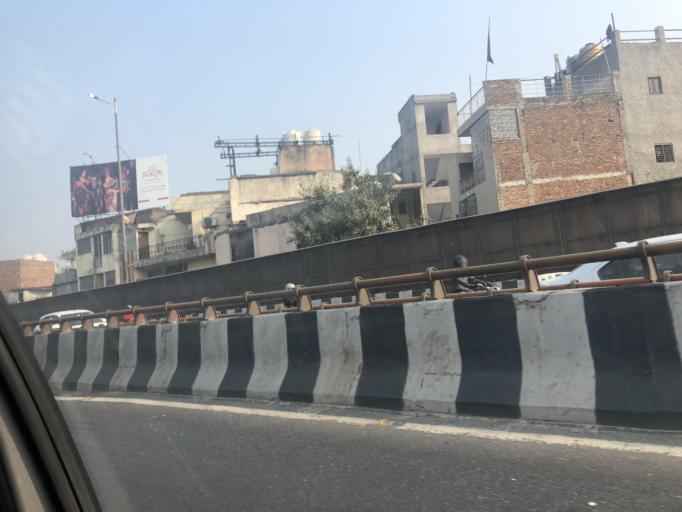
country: IN
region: NCT
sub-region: Central Delhi
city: Karol Bagh
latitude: 28.6210
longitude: 77.1363
